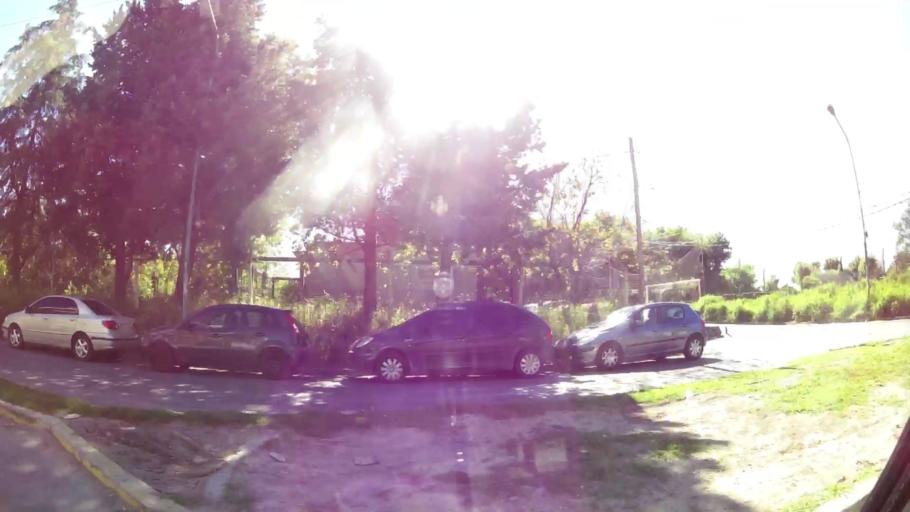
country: AR
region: Buenos Aires
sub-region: Partido de Vicente Lopez
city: Olivos
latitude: -34.5177
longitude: -58.4731
